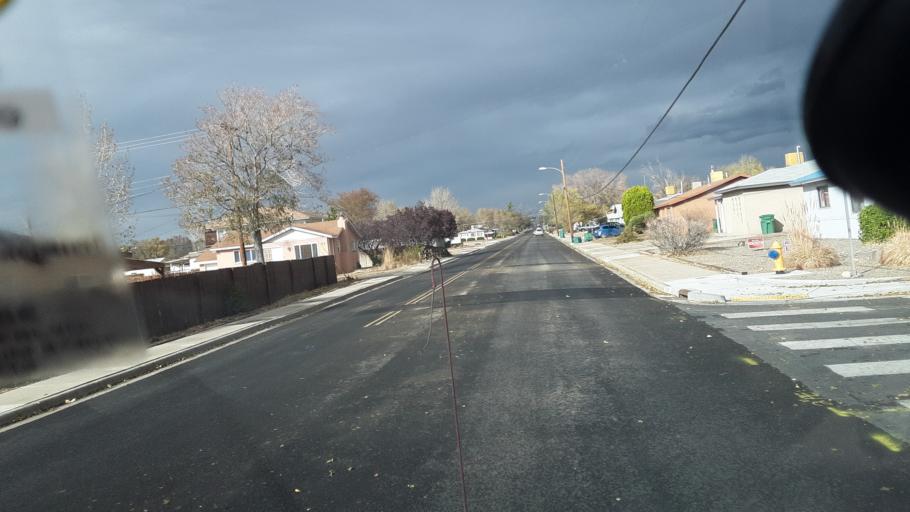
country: US
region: New Mexico
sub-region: San Juan County
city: Farmington
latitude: 36.7362
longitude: -108.1979
